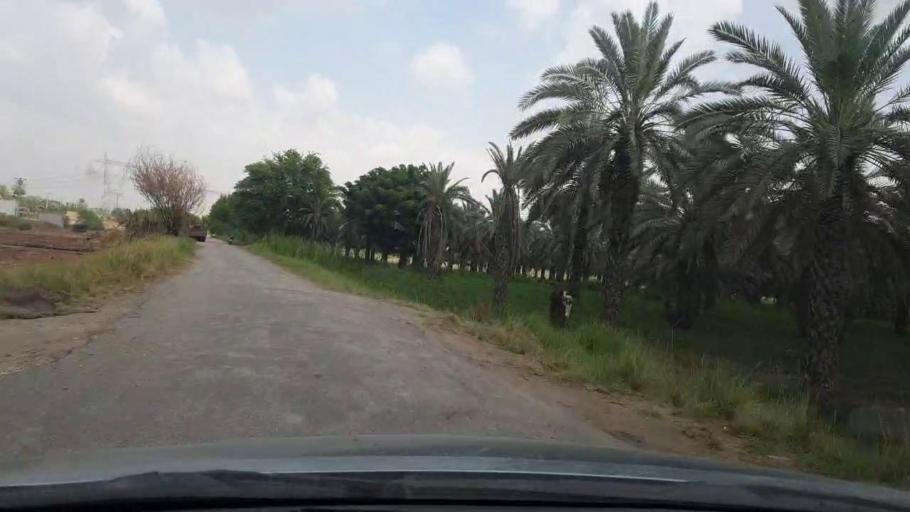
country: PK
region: Sindh
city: Khairpur
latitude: 27.4657
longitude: 68.7639
